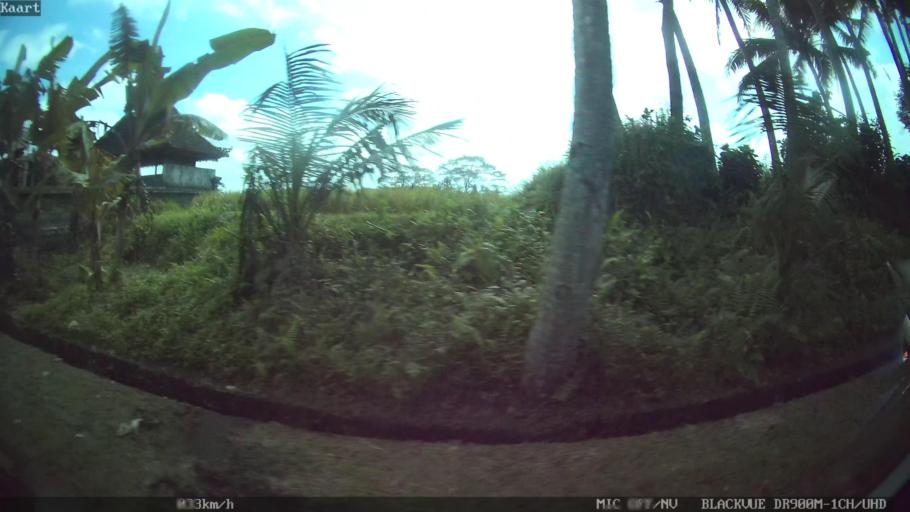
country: ID
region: Bali
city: Banjar Pesalakan
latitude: -8.5093
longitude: 115.3063
